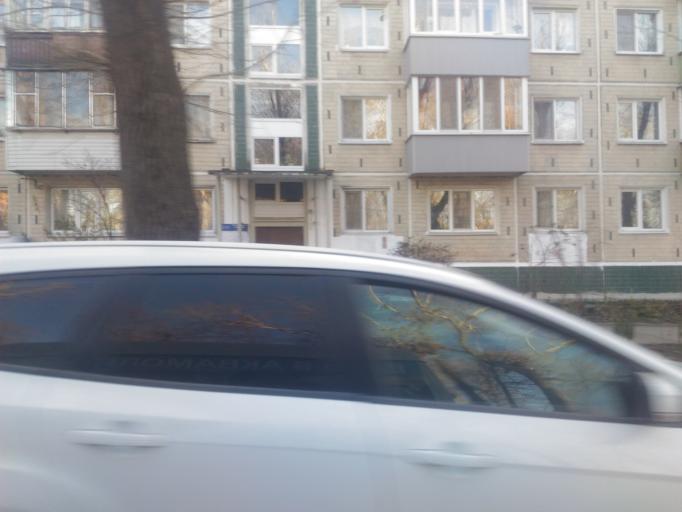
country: RU
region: Ulyanovsk
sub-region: Ulyanovskiy Rayon
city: Ulyanovsk
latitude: 54.3088
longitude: 48.3800
